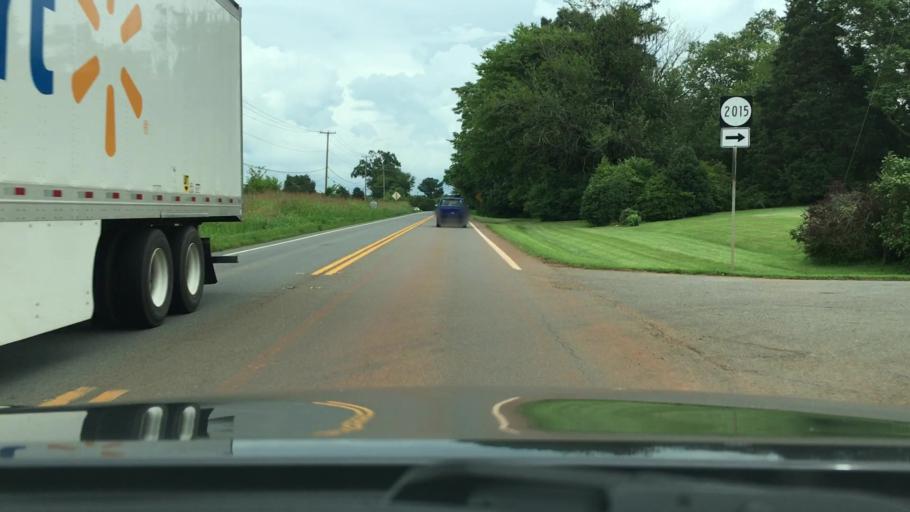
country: US
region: Virginia
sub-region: Orange County
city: Orange
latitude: 38.2445
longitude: -78.0771
